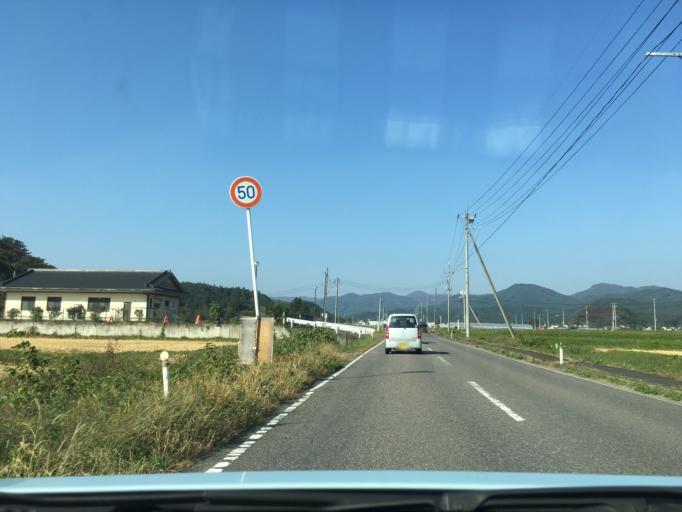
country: JP
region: Fukushima
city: Sukagawa
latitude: 37.2878
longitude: 140.2282
